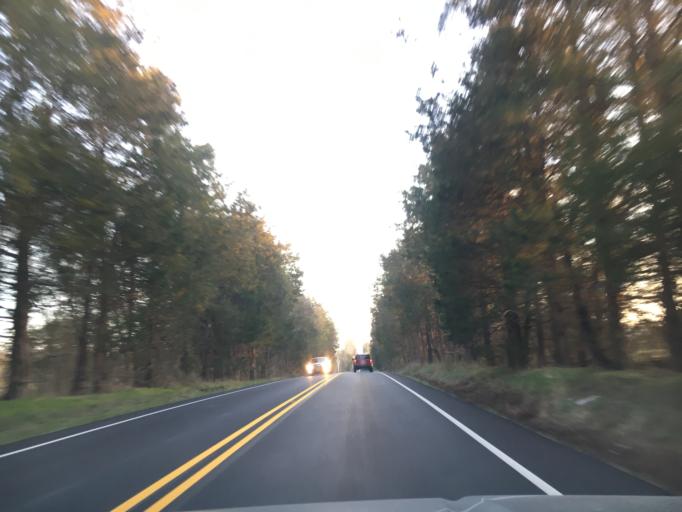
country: US
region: Virginia
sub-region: Orange County
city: Orange
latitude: 38.2077
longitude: -77.9445
